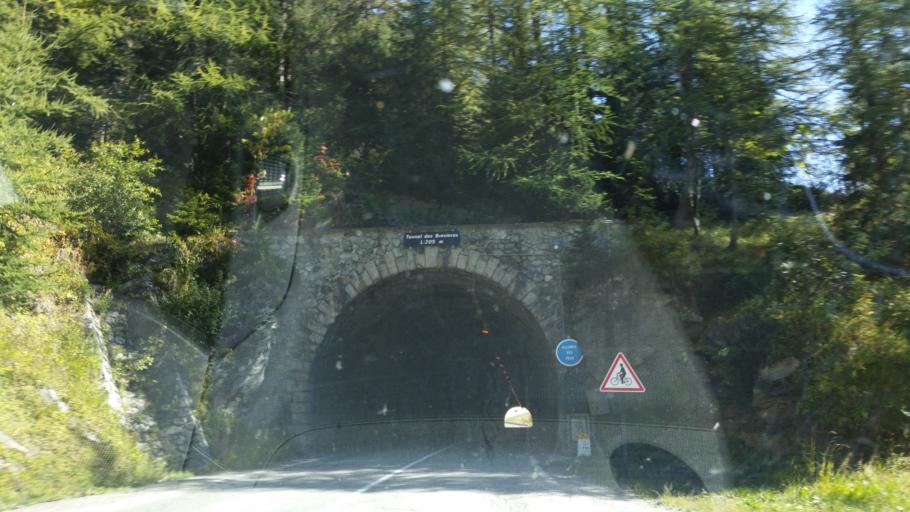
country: FR
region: Rhone-Alpes
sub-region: Departement de la Savoie
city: Tignes
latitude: 45.5069
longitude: 6.9263
